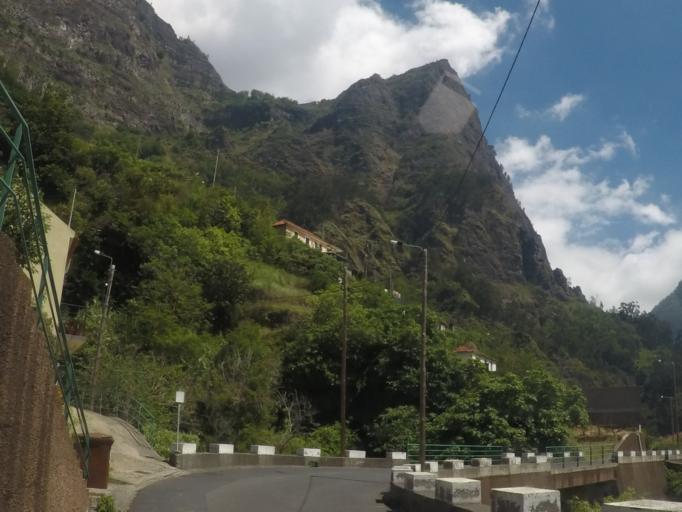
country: PT
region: Madeira
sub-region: Camara de Lobos
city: Curral das Freiras
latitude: 32.7178
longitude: -16.9684
